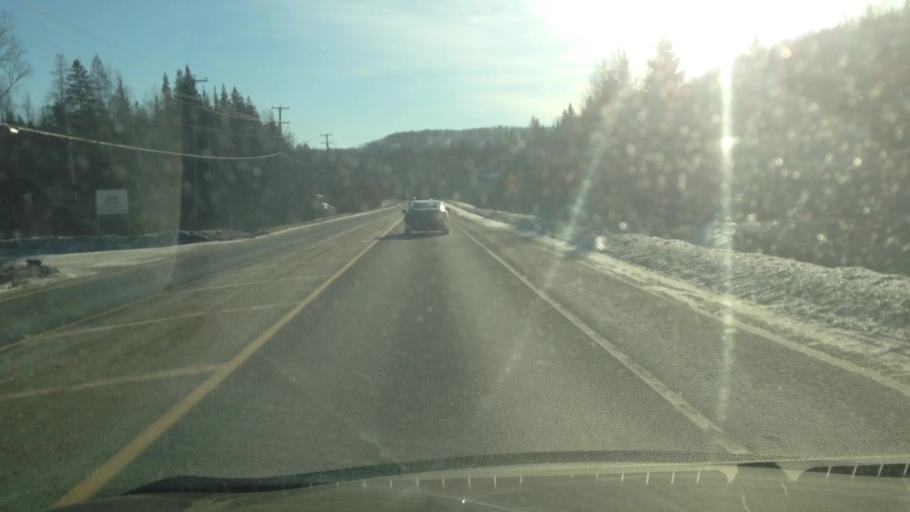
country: CA
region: Quebec
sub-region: Laurentides
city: Saint-Sauveur
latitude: 45.8892
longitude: -74.1908
